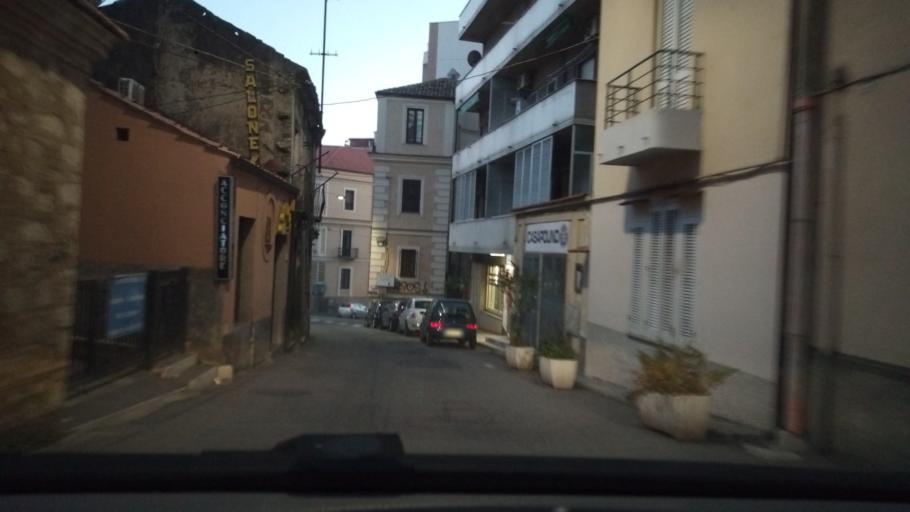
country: IT
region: Calabria
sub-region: Provincia di Catanzaro
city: Siano
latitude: 38.9128
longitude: 16.5871
